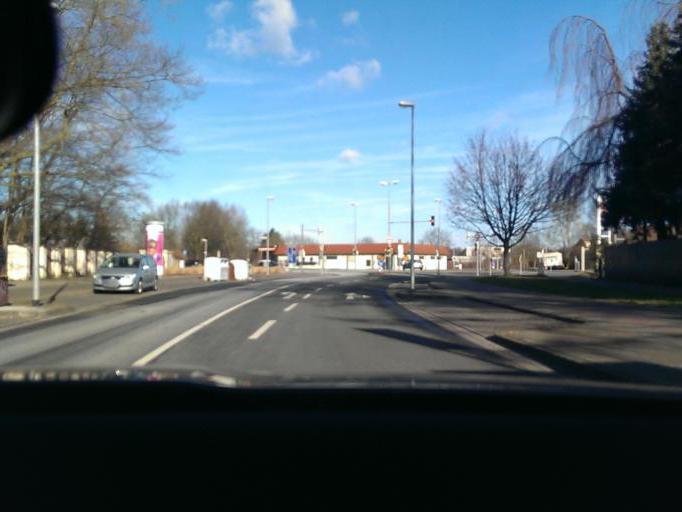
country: DE
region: Lower Saxony
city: Langenhagen
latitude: 52.4240
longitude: 9.7814
